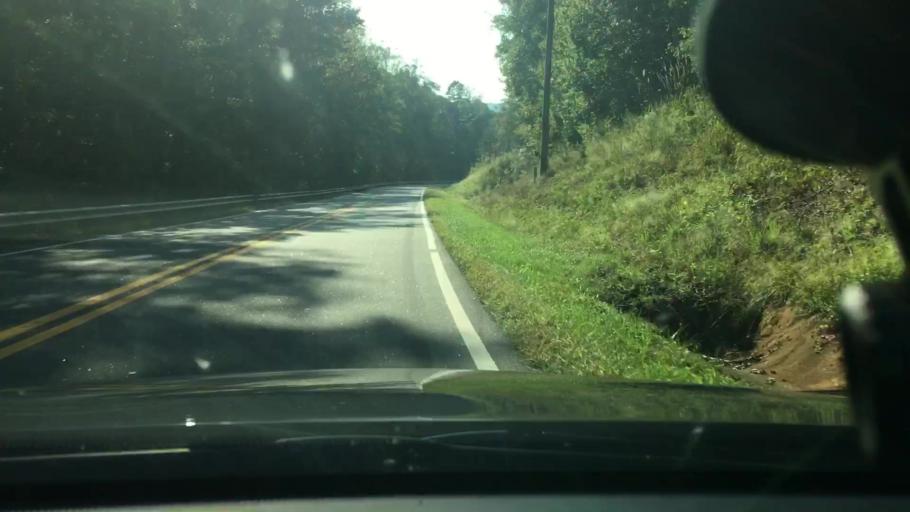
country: US
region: North Carolina
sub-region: Rutherford County
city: Rutherfordton
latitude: 35.3272
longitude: -82.0644
